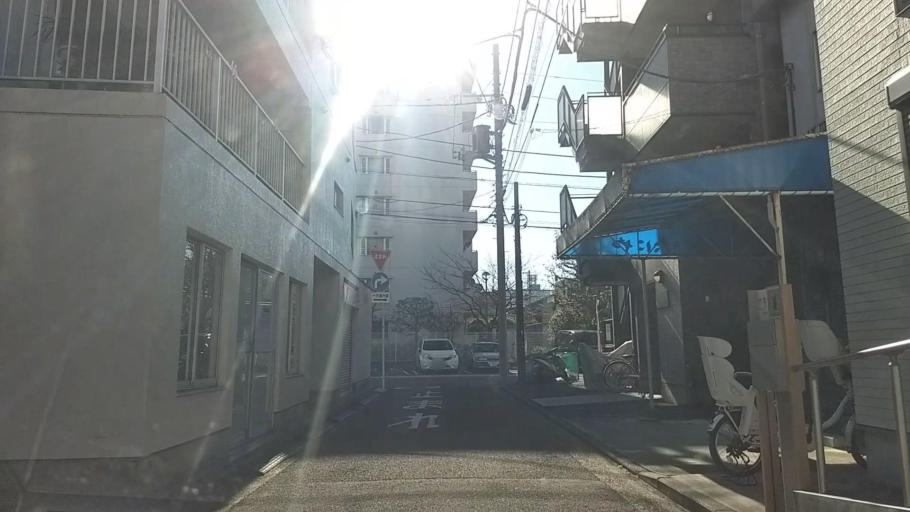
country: JP
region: Kanagawa
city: Yokohama
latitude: 35.4551
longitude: 139.6073
